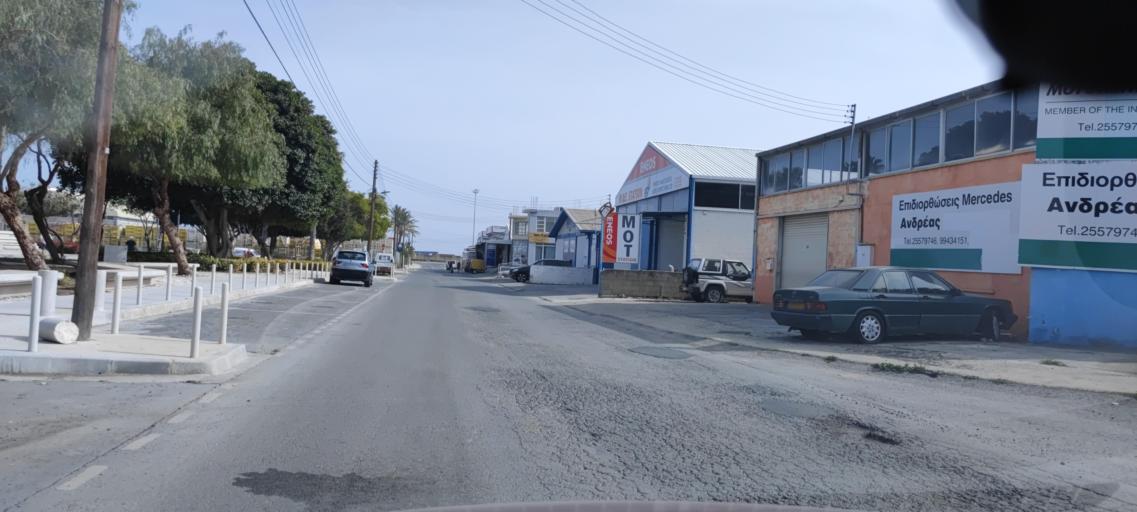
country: CY
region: Limassol
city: Limassol
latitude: 34.6625
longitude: 33.0210
